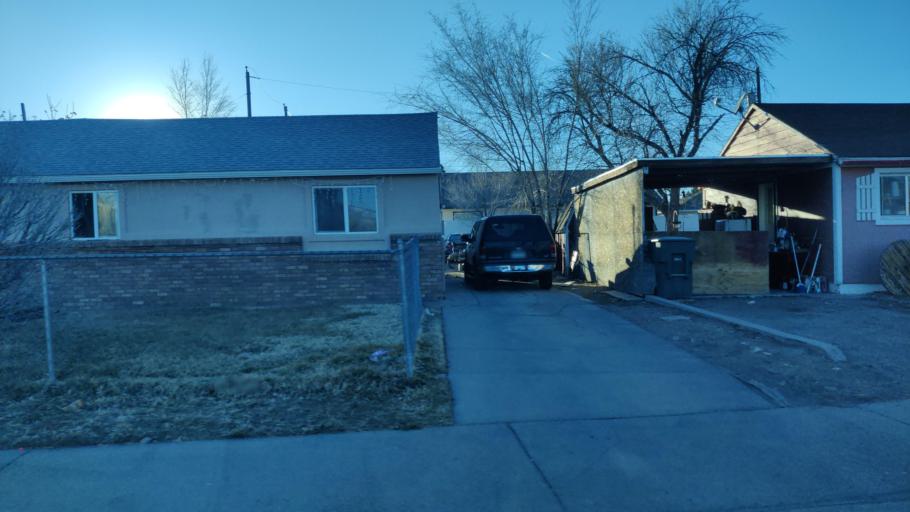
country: US
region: Colorado
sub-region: Mesa County
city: Grand Junction
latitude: 39.0853
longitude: -108.5373
